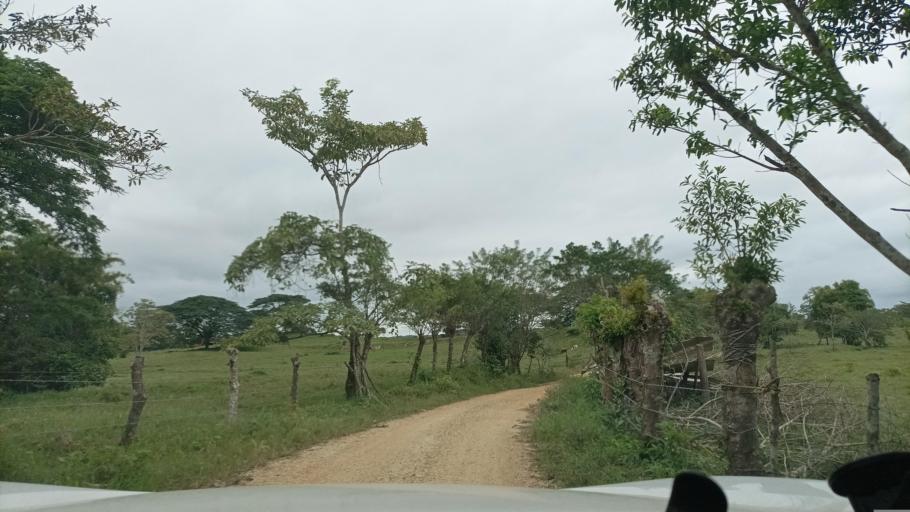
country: MX
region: Veracruz
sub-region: Uxpanapa
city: Poblado Cinco
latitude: 17.5067
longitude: -94.5628
